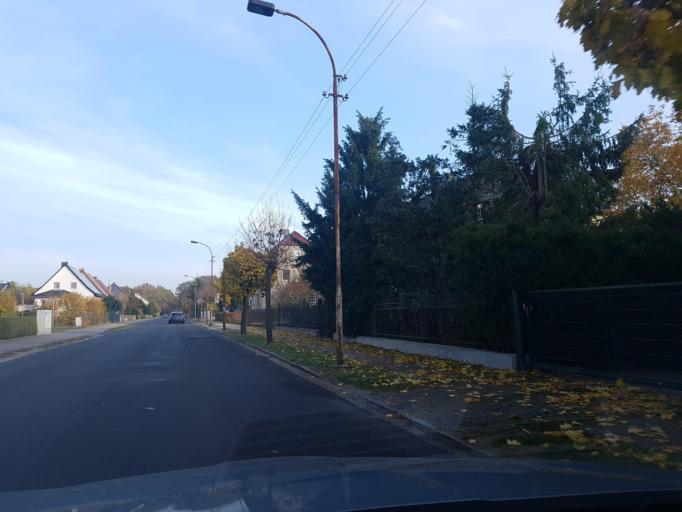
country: DE
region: Brandenburg
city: Falkenberg
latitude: 51.5878
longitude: 13.2609
